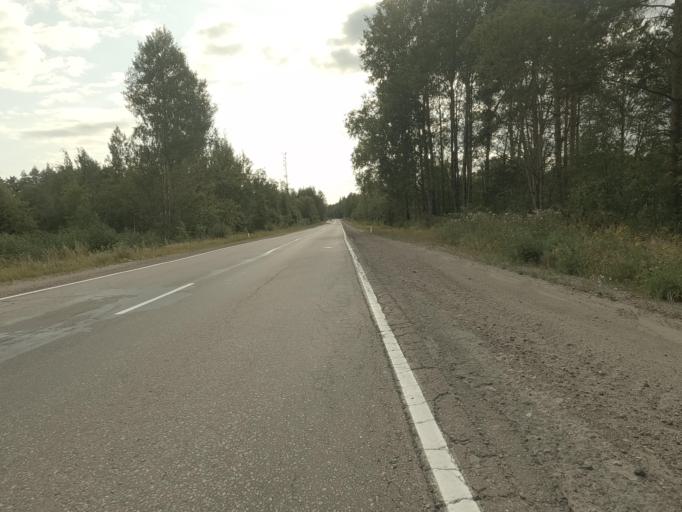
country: RU
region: Leningrad
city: Kamennogorsk
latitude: 60.8790
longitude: 29.0187
